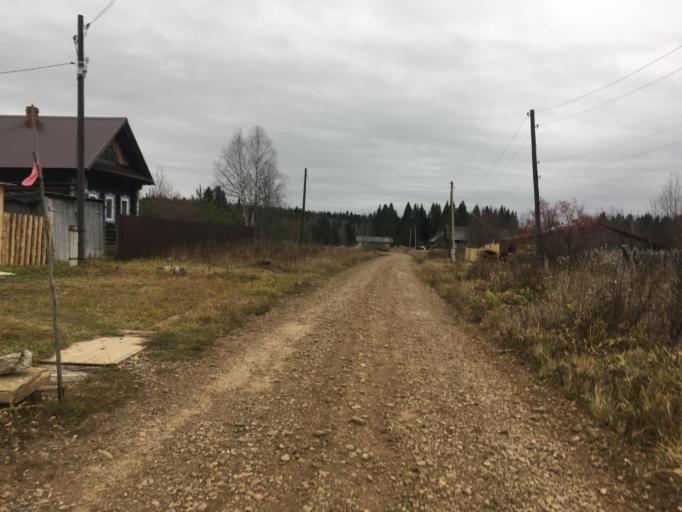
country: RU
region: Perm
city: Komarikhinskiy
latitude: 58.0894
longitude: 57.1098
